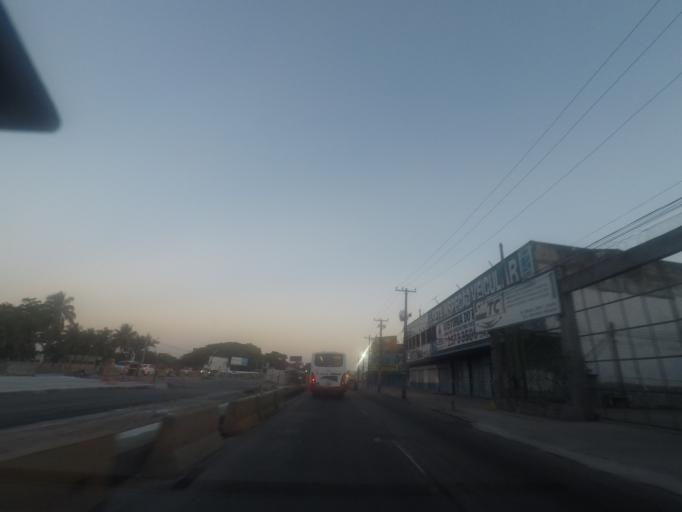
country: BR
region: Rio de Janeiro
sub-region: Duque De Caxias
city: Duque de Caxias
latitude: -22.8377
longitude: -43.2571
